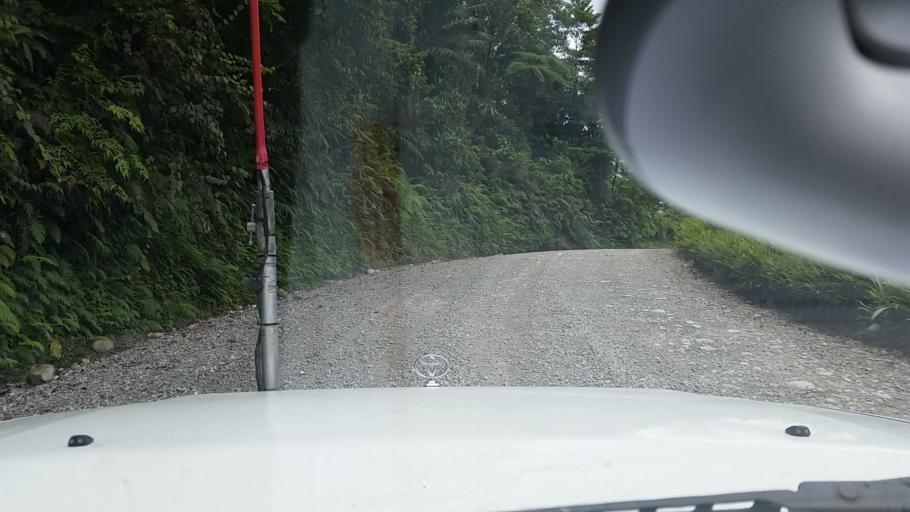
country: PG
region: Western Province
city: Kiunga
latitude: -5.5738
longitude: 141.2514
